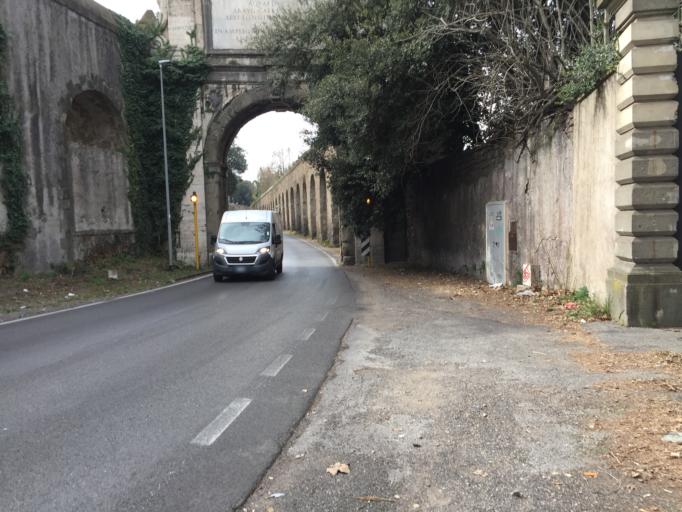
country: VA
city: Vatican City
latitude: 41.8890
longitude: 12.4535
